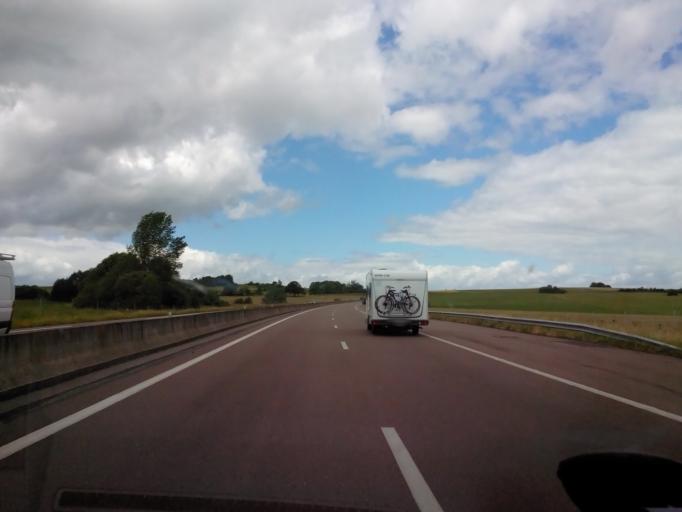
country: FR
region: Lorraine
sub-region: Departement des Vosges
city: Chatenois
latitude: 48.3913
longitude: 5.8799
